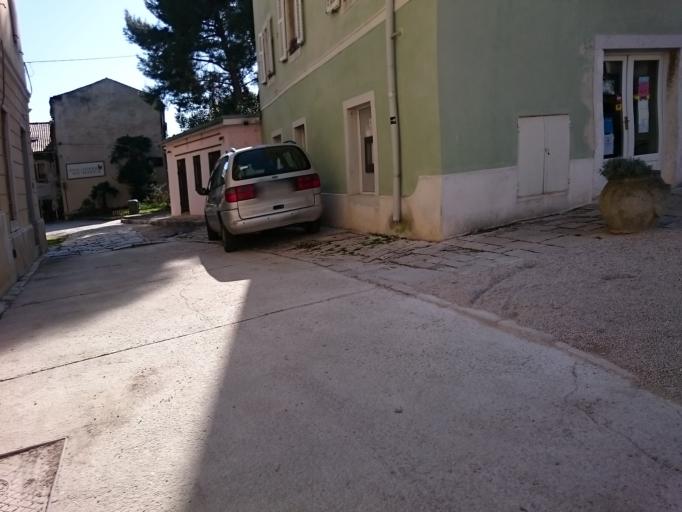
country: HR
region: Istarska
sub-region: Grad Porec
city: Porec
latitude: 45.2282
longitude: 13.5907
